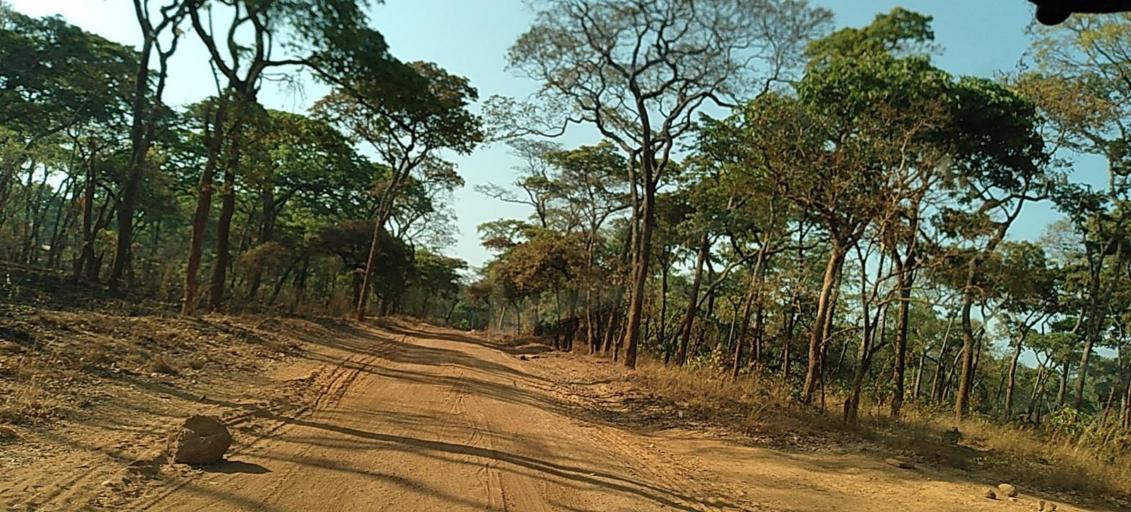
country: ZM
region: North-Western
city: Kasempa
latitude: -13.5560
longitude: 25.9990
